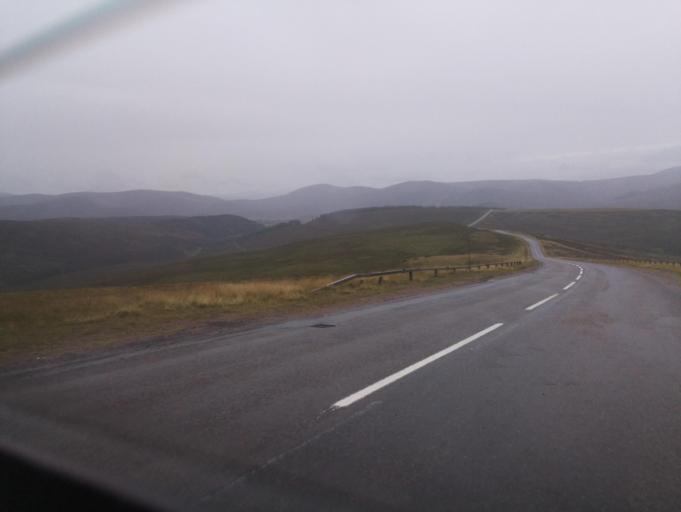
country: GB
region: Scotland
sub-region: Aberdeenshire
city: Ballater
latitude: 57.1887
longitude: -3.2390
